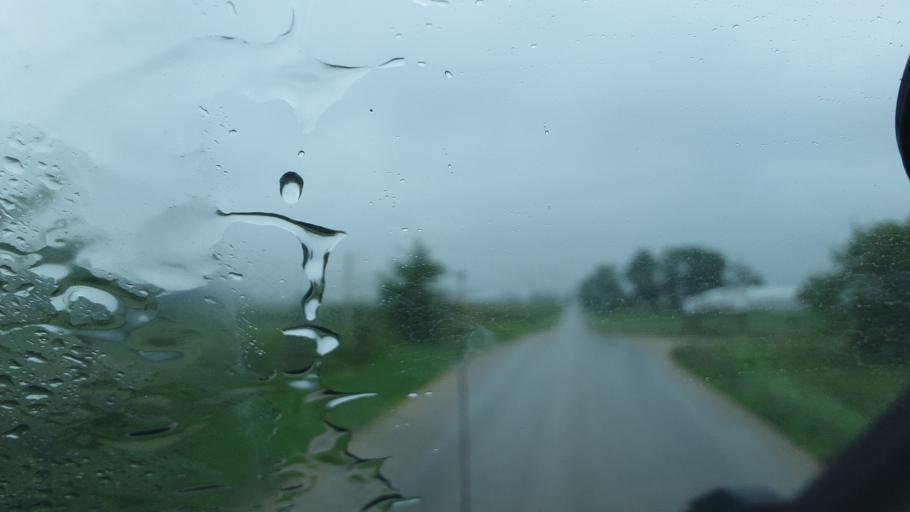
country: US
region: Indiana
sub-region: Adams County
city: Berne
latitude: 40.6742
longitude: -84.8360
